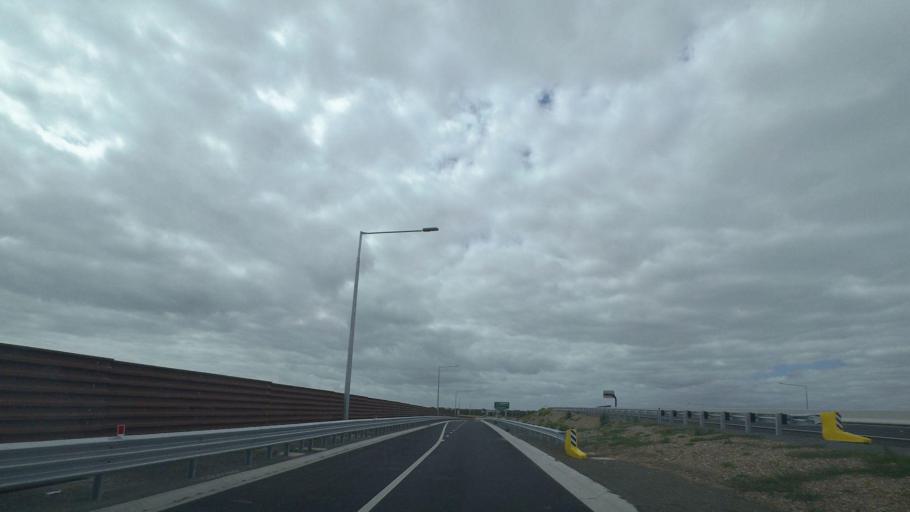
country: AU
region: Victoria
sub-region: Kingston
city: Waterways
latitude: -38.0128
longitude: 145.1231
